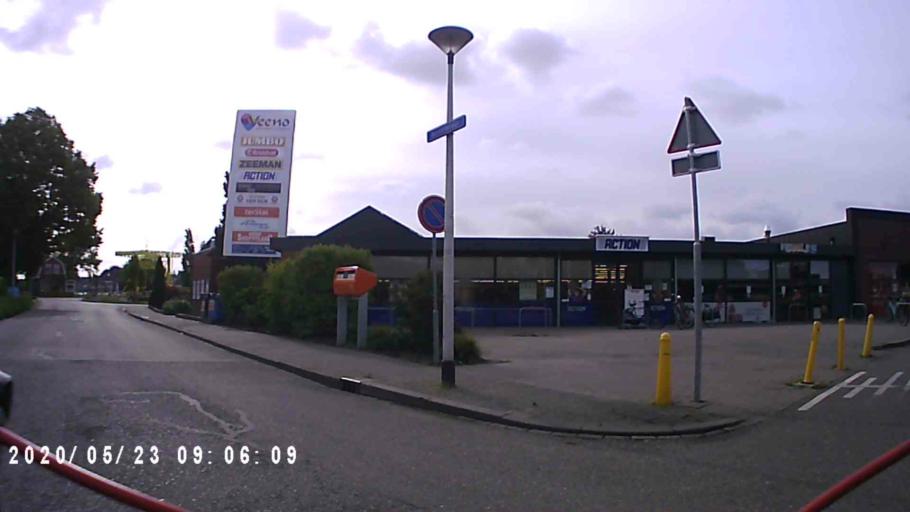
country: NL
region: Groningen
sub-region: Gemeente Bedum
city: Bedum
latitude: 53.3004
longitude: 6.5950
